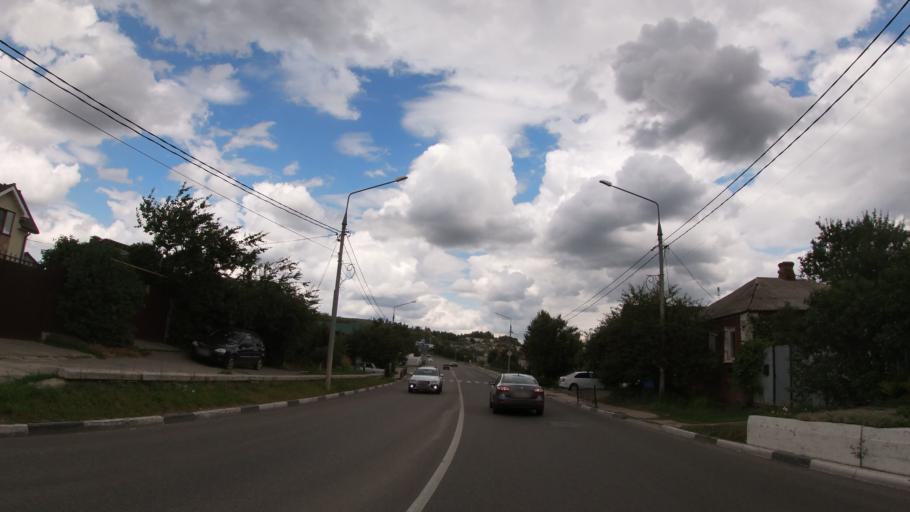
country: RU
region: Belgorod
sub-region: Belgorodskiy Rayon
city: Belgorod
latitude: 50.6071
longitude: 36.6127
